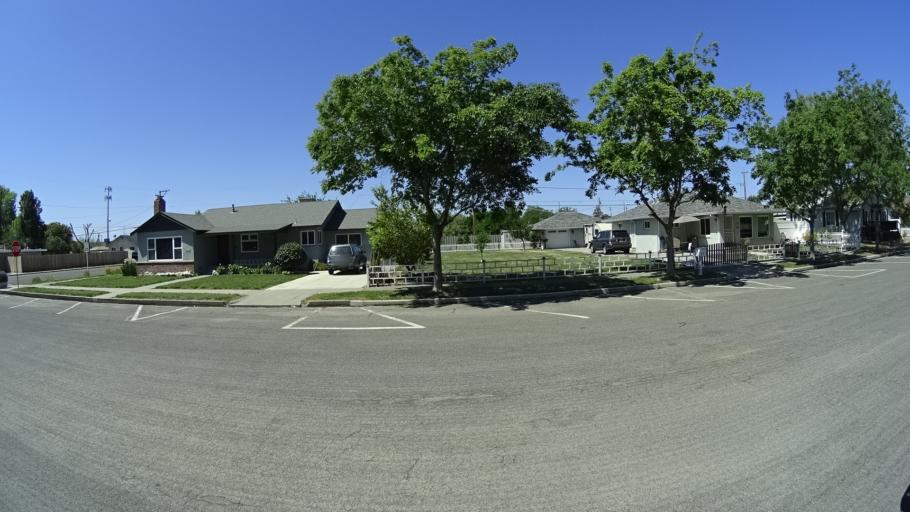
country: US
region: California
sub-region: Glenn County
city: Orland
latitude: 39.7524
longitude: -122.1940
